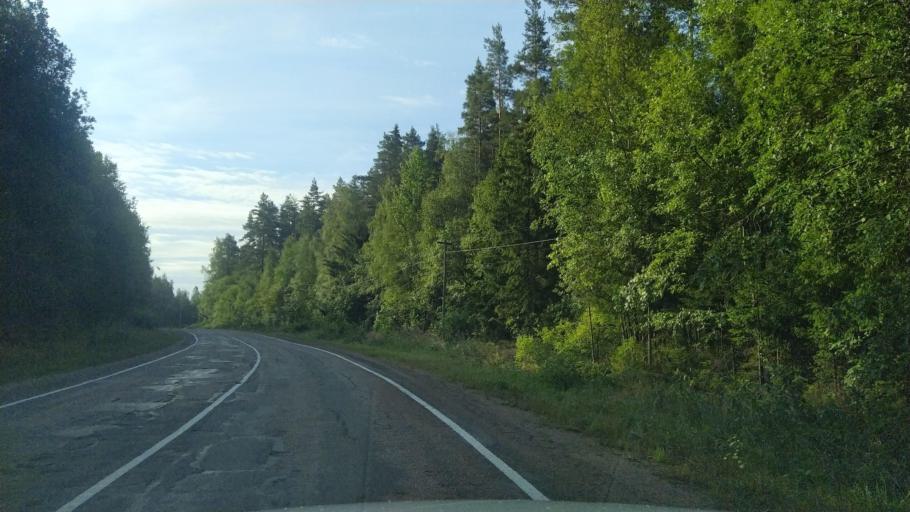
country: RU
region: Leningrad
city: Priozersk
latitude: 60.9895
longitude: 30.2586
